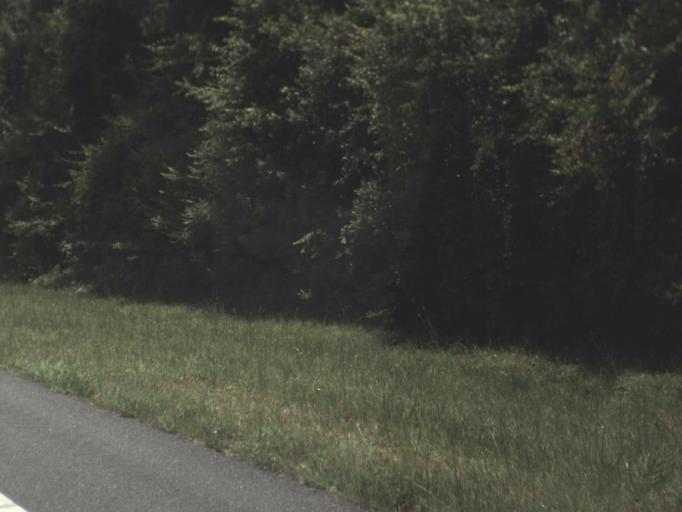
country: US
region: Florida
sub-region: Dixie County
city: Cross City
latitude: 29.6576
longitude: -82.9840
